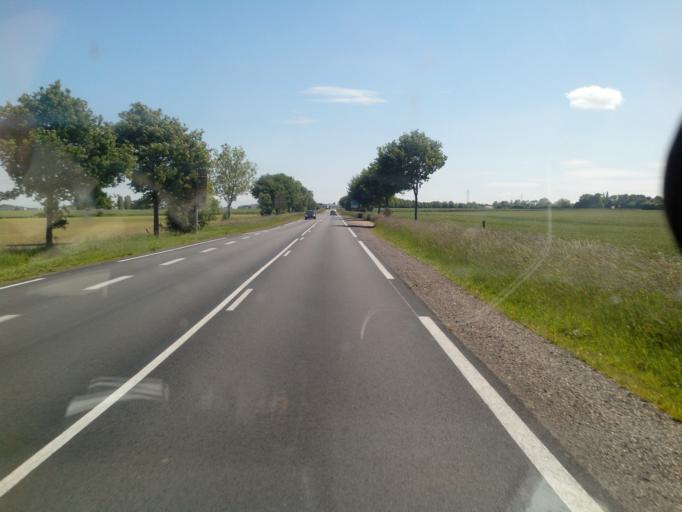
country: FR
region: Haute-Normandie
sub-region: Departement de l'Eure
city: Beuzeville
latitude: 49.3653
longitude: 0.3952
